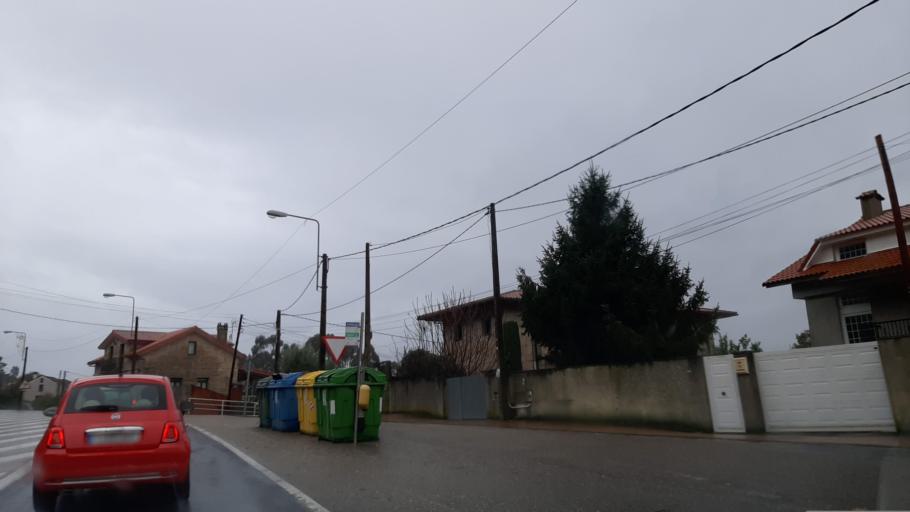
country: ES
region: Galicia
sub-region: Provincia de Pontevedra
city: Nigran
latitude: 42.1832
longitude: -8.7890
